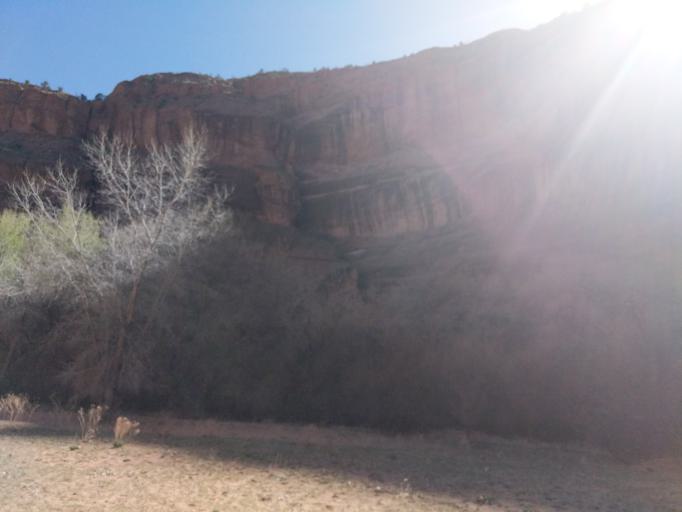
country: US
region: Arizona
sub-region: Apache County
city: Chinle
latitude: 36.1565
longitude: -109.4500
